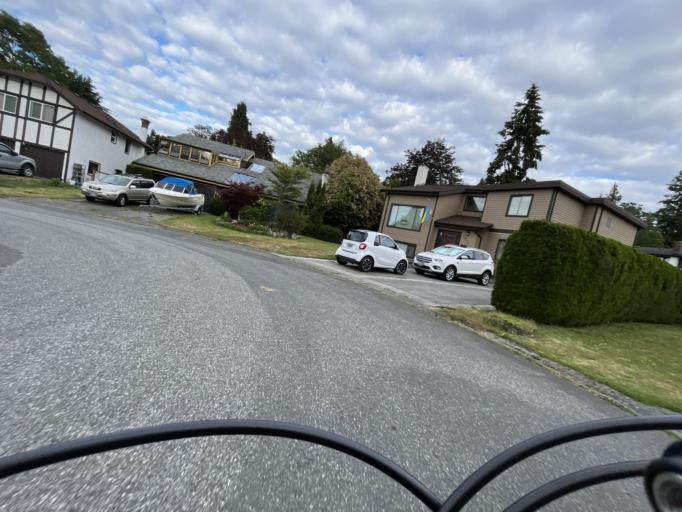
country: CA
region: British Columbia
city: Oak Bay
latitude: 48.4830
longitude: -123.3405
